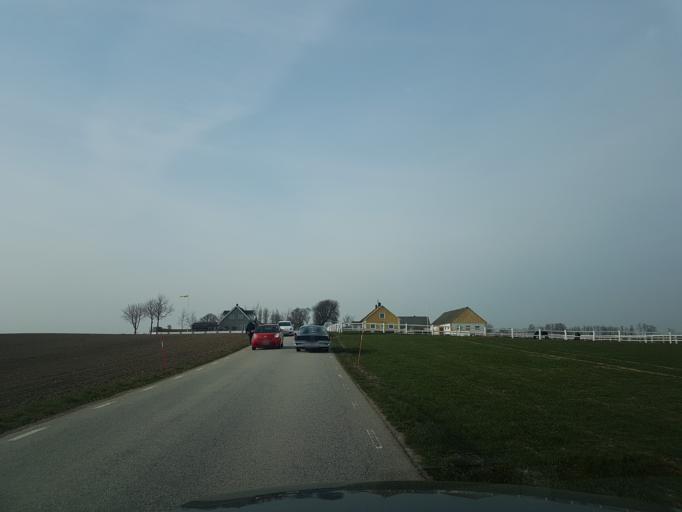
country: SE
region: Skane
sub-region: Ystads Kommun
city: Ystad
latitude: 55.4567
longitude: 13.8286
